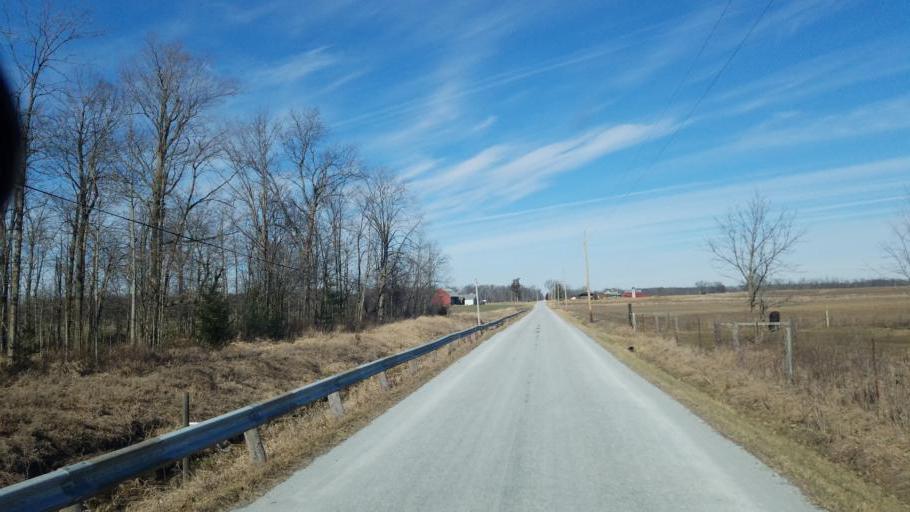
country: US
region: Ohio
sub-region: Hardin County
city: Kenton
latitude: 40.5901
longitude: -83.4757
